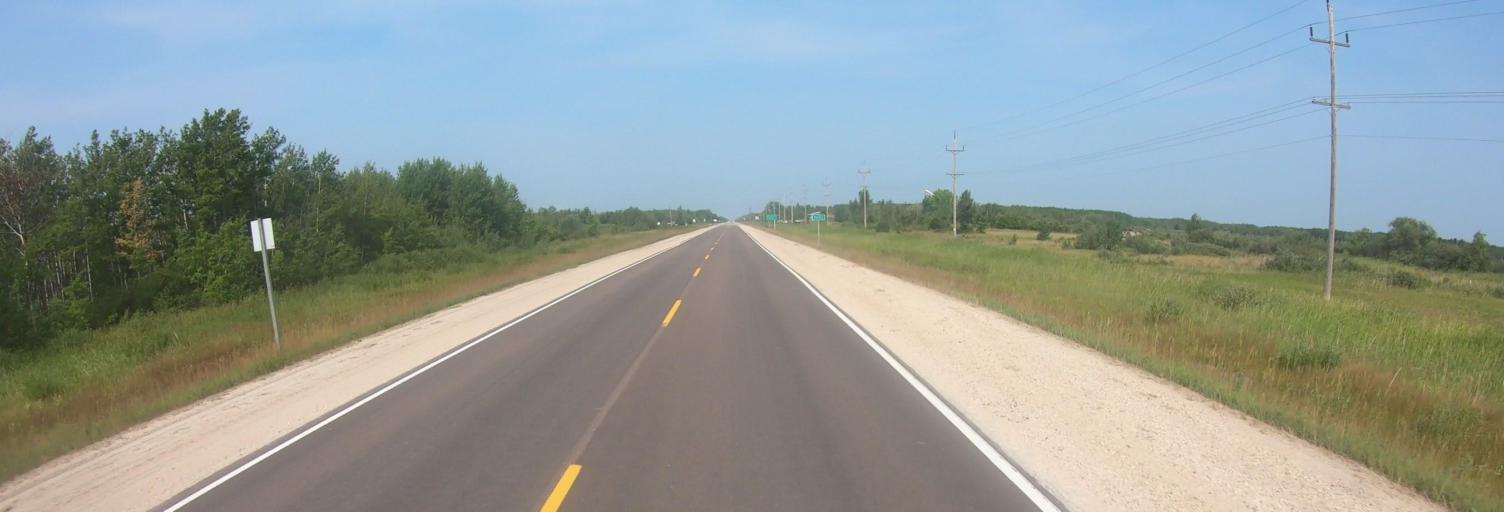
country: CA
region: Manitoba
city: La Broquerie
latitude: 49.2813
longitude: -96.5052
